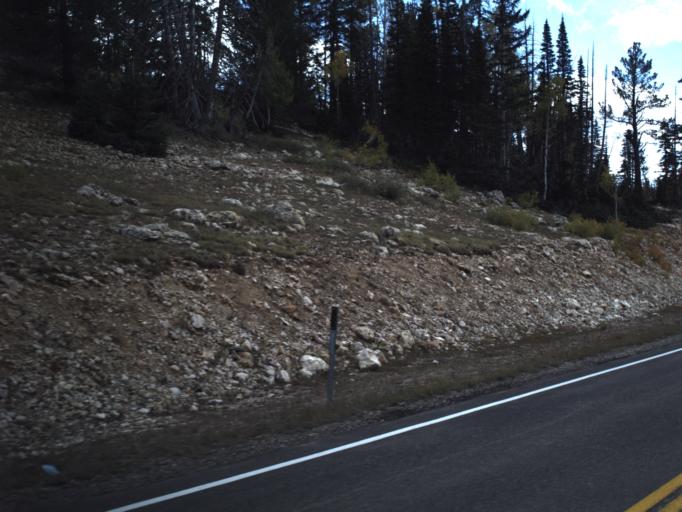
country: US
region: Utah
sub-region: Iron County
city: Parowan
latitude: 37.5434
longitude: -112.7849
